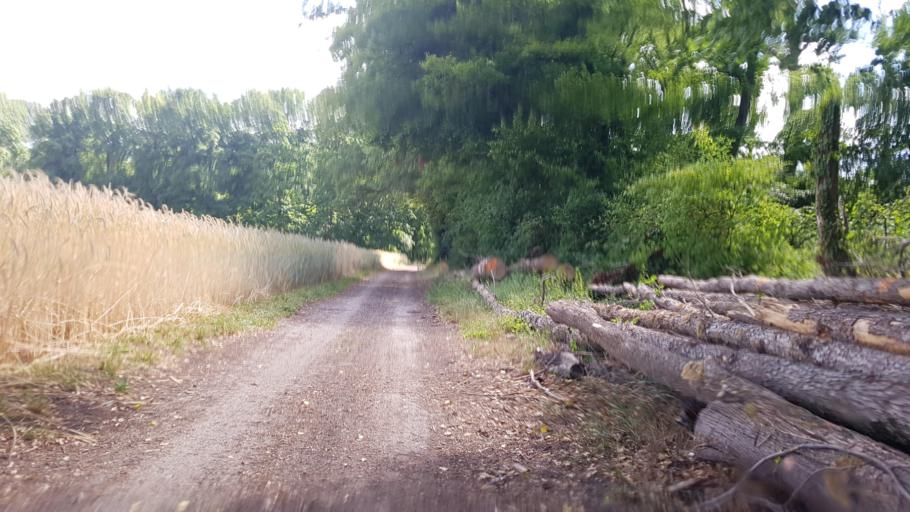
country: DE
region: Baden-Wuerttemberg
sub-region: Karlsruhe Region
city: Weingarten
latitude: 49.0796
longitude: 8.5377
